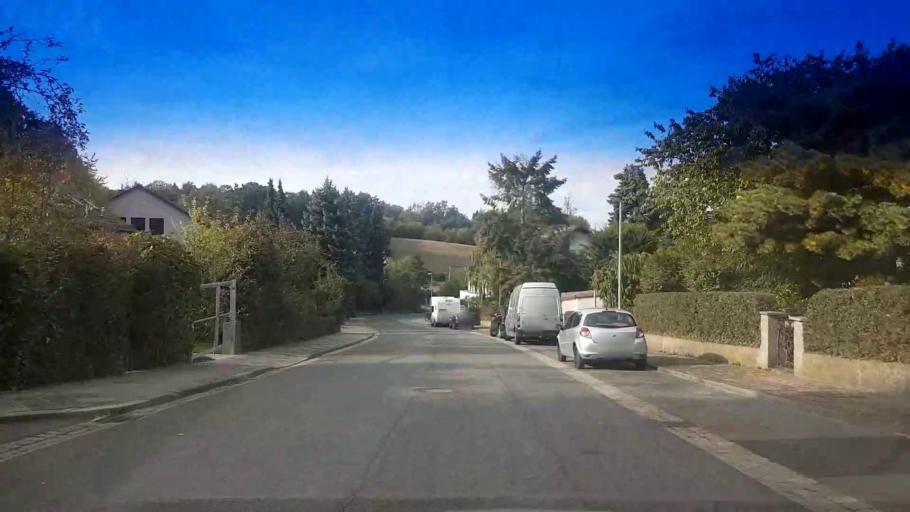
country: DE
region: Bavaria
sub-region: Upper Franconia
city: Bamberg
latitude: 49.8798
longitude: 10.8791
